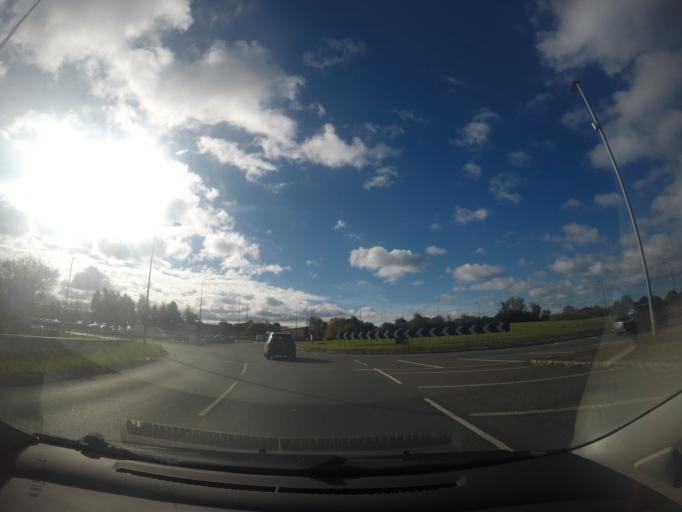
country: GB
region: England
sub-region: City of York
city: Nether Poppleton
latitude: 53.9794
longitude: -1.1357
